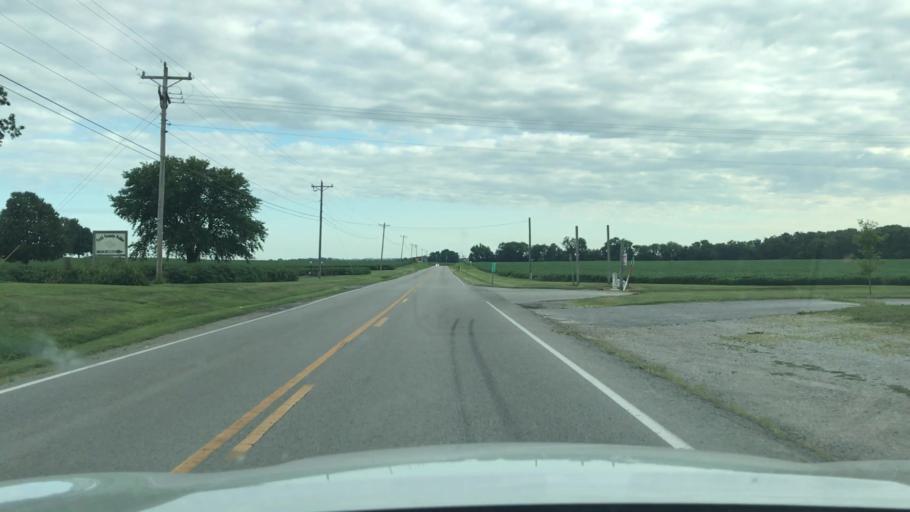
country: US
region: Kentucky
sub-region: Todd County
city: Elkton
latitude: 36.7654
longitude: -87.1670
